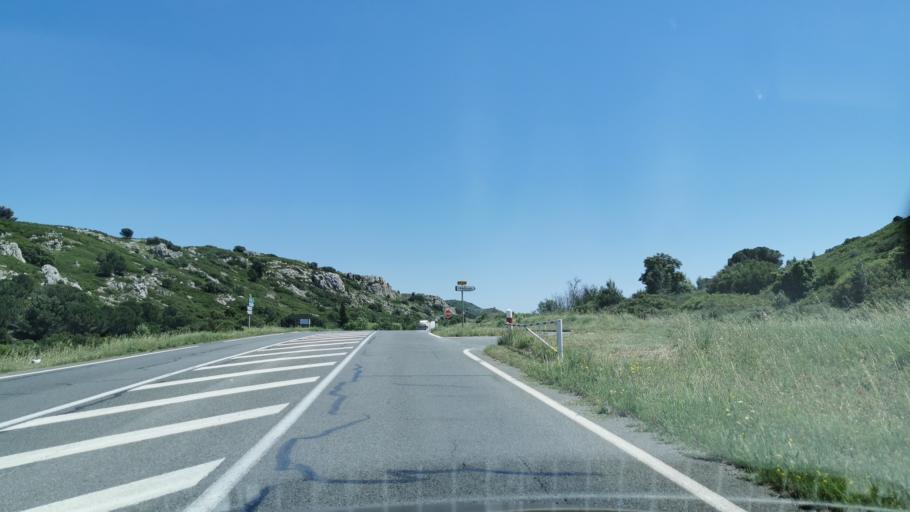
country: FR
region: Languedoc-Roussillon
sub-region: Departement de l'Aude
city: Nevian
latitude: 43.2071
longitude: 2.8833
